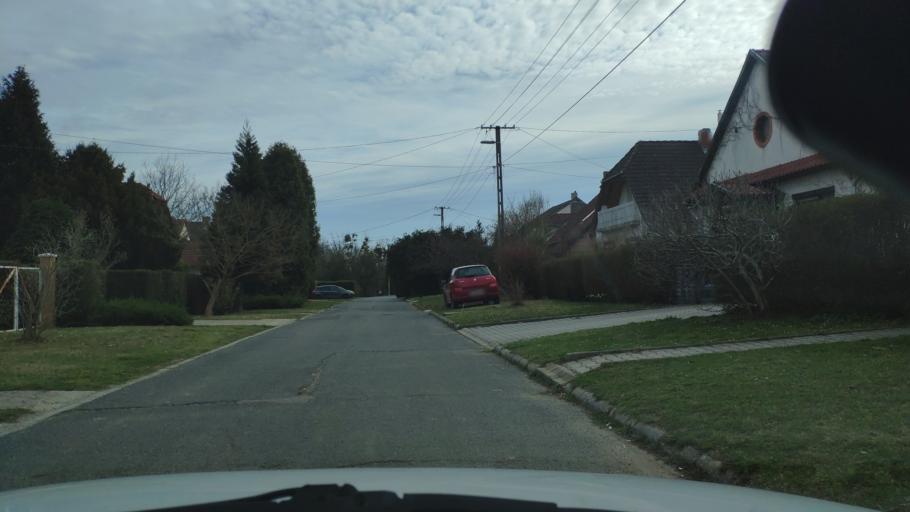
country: HU
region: Zala
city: Nagykanizsa
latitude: 46.4826
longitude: 16.9904
